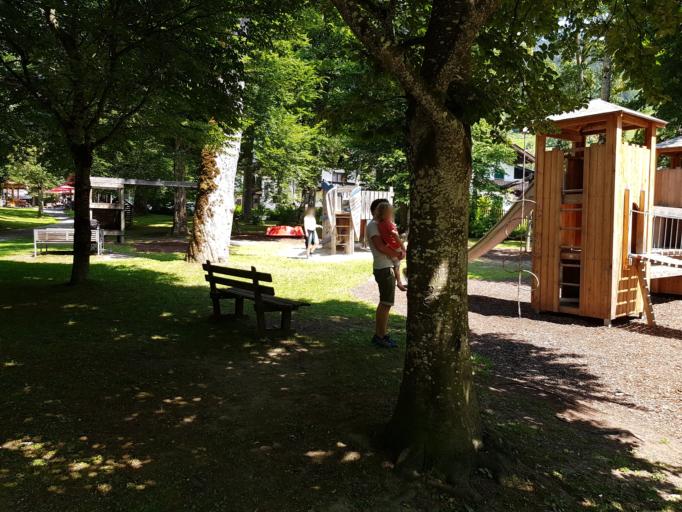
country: AT
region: Salzburg
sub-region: Politischer Bezirk Zell am See
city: Zell am See
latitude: 47.3296
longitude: 12.8147
